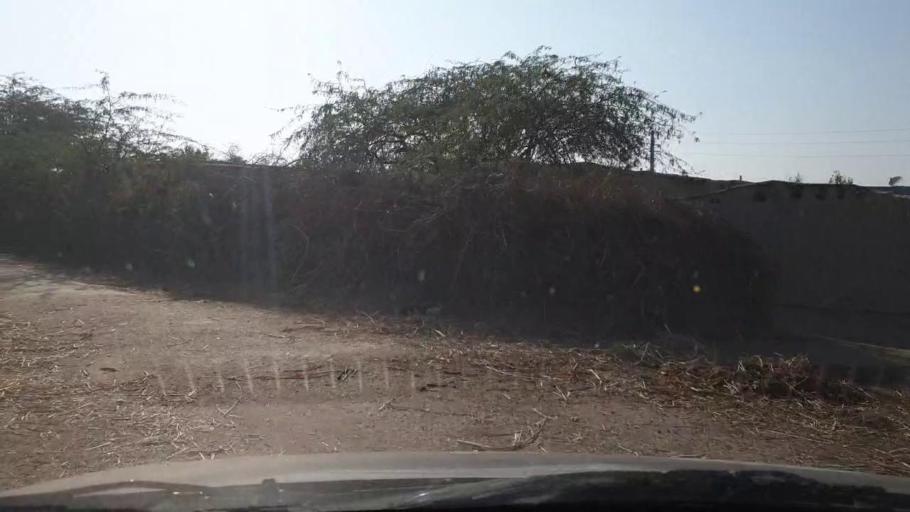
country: PK
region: Sindh
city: Samaro
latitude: 25.1678
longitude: 69.2807
